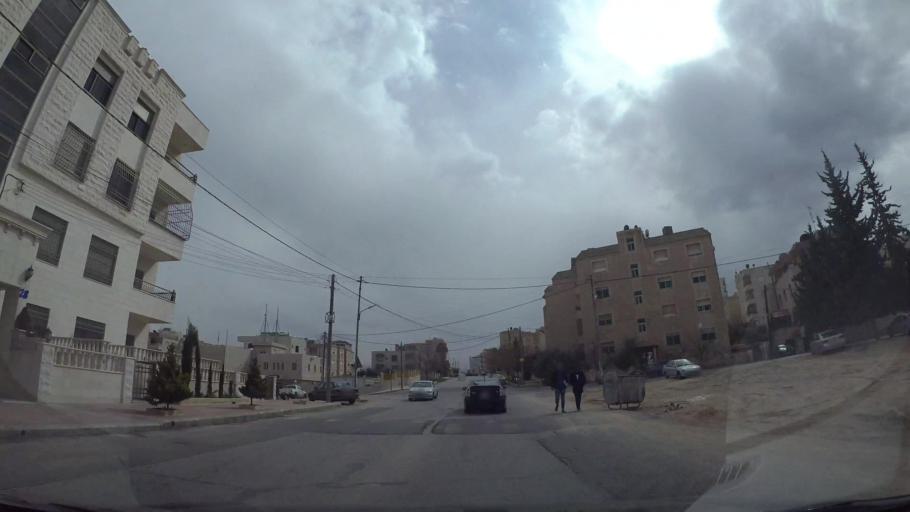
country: JO
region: Amman
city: Amman
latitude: 31.9944
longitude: 35.9425
